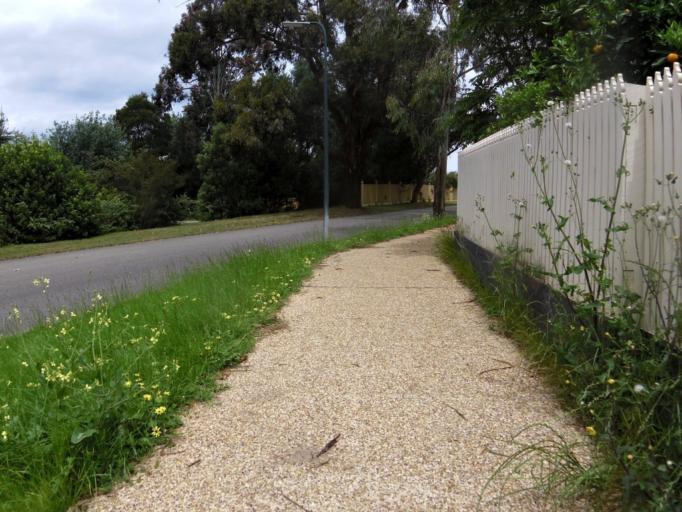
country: AU
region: Victoria
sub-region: Cardinia
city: Gembrook
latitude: -37.9510
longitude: 145.5483
